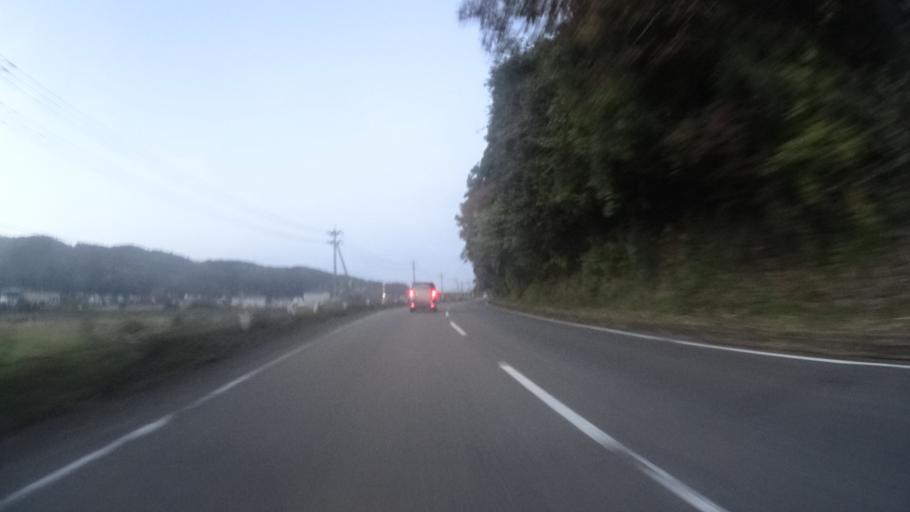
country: JP
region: Ishikawa
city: Nanao
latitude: 37.3743
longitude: 136.8798
